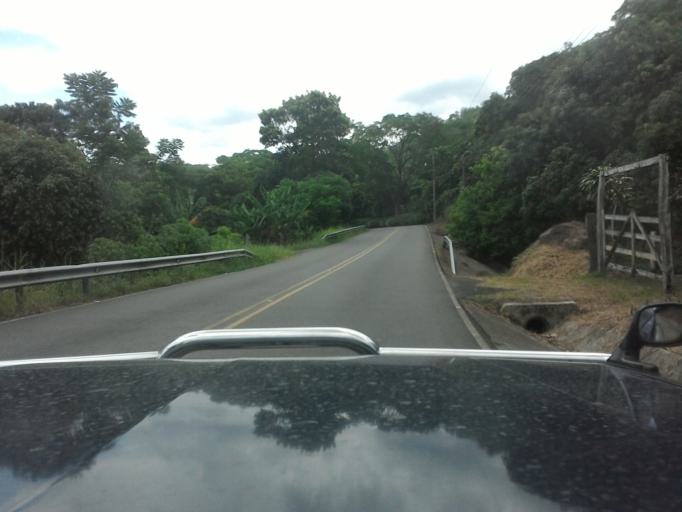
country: CR
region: Guanacaste
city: Juntas
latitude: 10.1927
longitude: -84.8427
